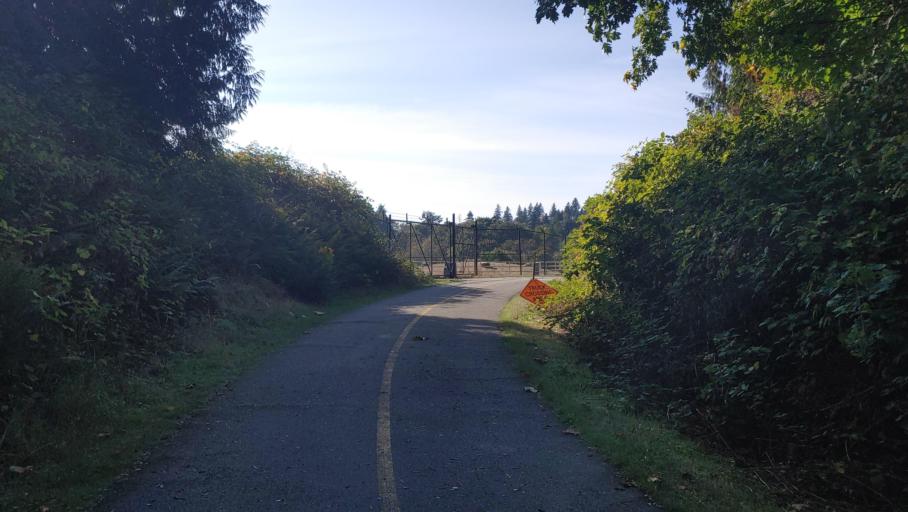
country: US
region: Washington
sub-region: King County
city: Des Moines
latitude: 47.4114
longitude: -122.3164
